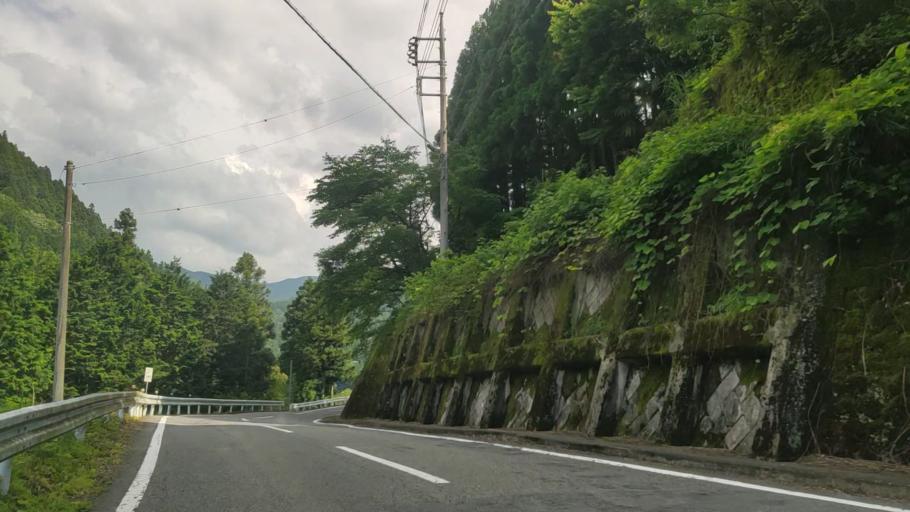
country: JP
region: Gunma
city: Tomioka
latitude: 36.1548
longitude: 138.7281
